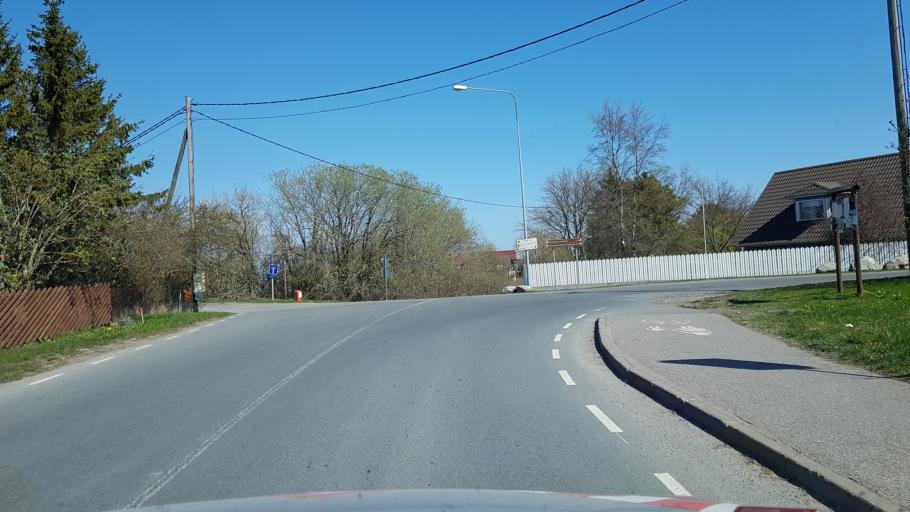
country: EE
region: Harju
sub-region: Viimsi vald
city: Rummu
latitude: 59.5616
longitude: 24.8005
